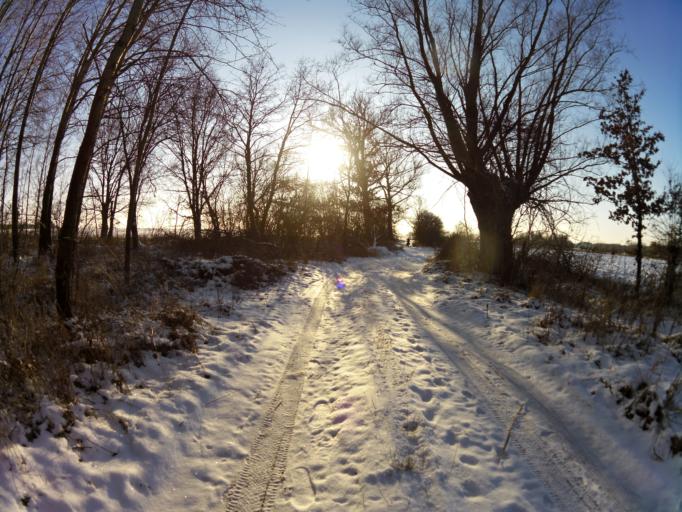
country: PL
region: West Pomeranian Voivodeship
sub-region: Powiat stargardzki
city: Dobrzany
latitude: 53.3384
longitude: 15.4115
